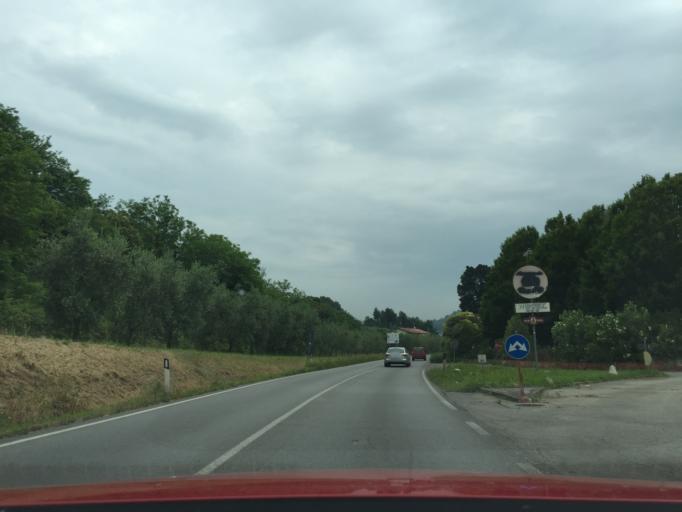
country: IT
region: Tuscany
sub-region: Provincia di Pistoia
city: Pieve a Nievole
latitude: 43.8864
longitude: 10.8108
